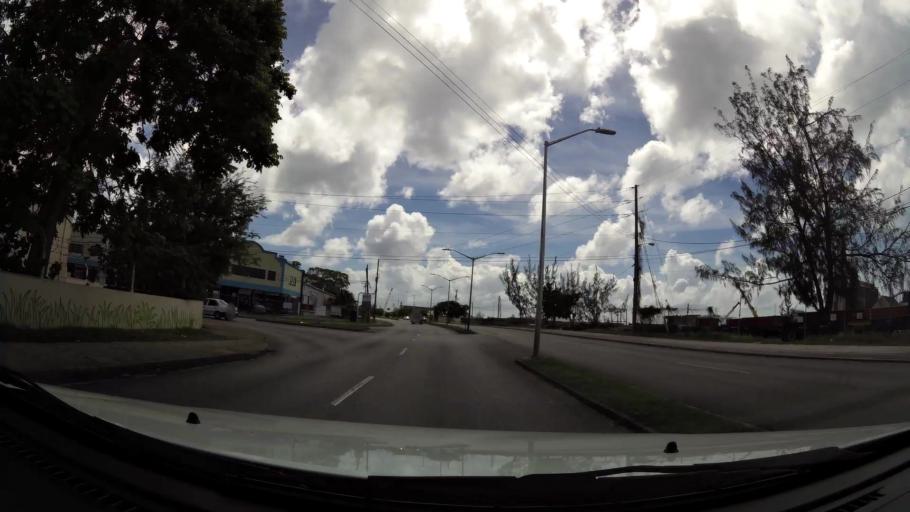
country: BB
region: Saint Michael
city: Bridgetown
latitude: 13.1121
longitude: -59.6269
